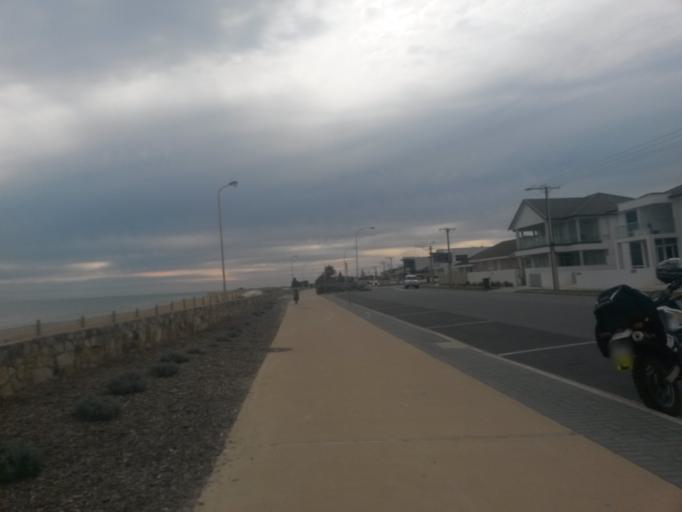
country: AU
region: South Australia
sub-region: Charles Sturt
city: Henley Beach
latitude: -34.9452
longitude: 138.5012
